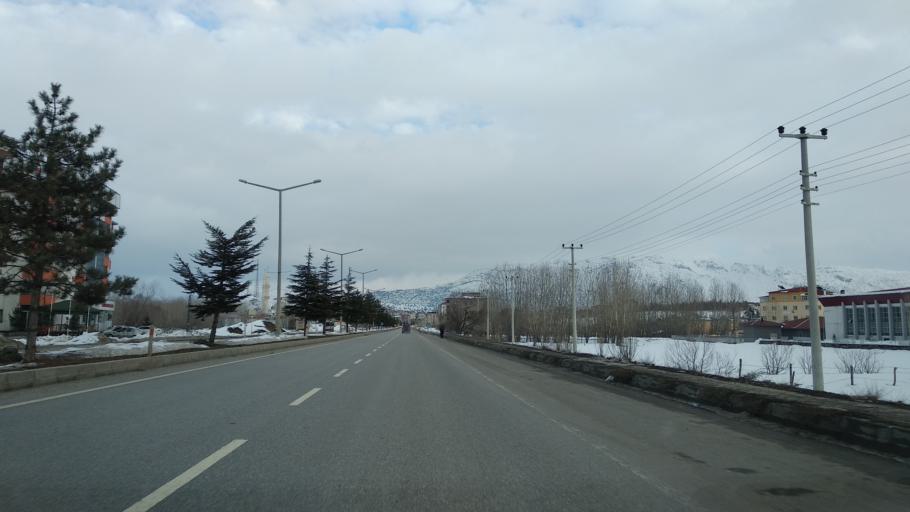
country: TR
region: Kahramanmaras
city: Goksun
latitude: 38.0266
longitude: 36.4884
